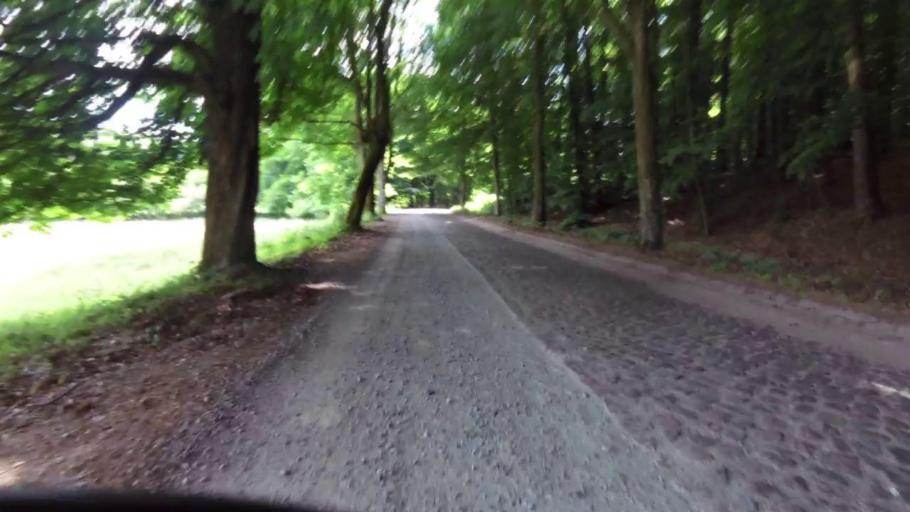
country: PL
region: West Pomeranian Voivodeship
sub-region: Powiat kamienski
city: Miedzyzdroje
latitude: 53.8778
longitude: 14.4597
